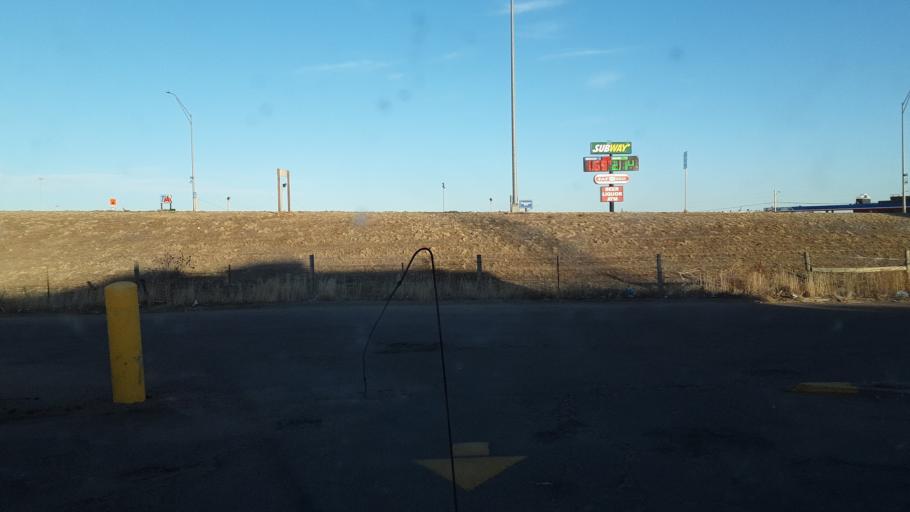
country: US
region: Nebraska
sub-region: Keith County
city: Ogallala
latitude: 41.1130
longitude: -101.7163
